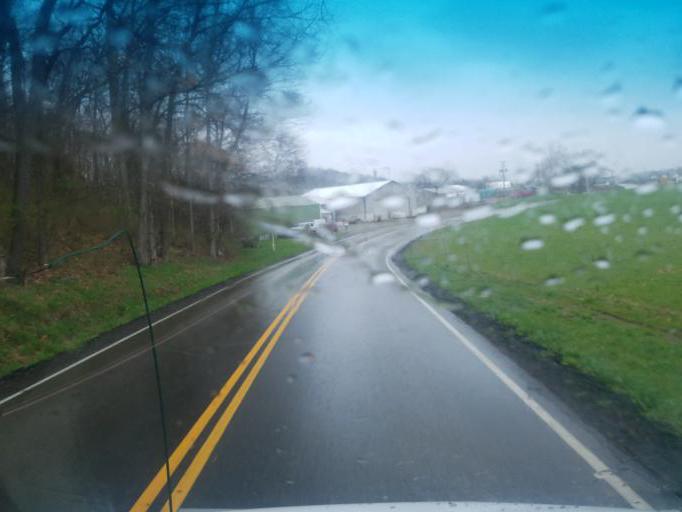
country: US
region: Ohio
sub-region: Holmes County
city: Millersburg
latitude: 40.6276
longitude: -81.9022
